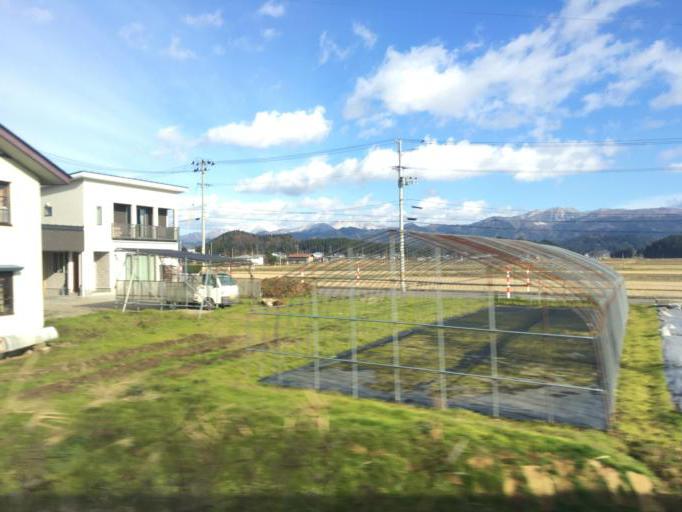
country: JP
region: Akita
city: Yokotemachi
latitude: 39.3728
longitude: 140.5340
